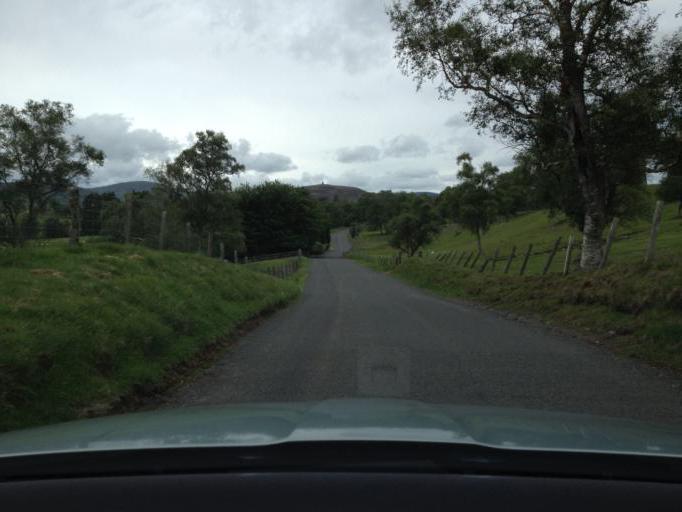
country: GB
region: Scotland
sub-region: Aberdeenshire
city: Aboyne
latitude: 56.9002
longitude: -2.8177
